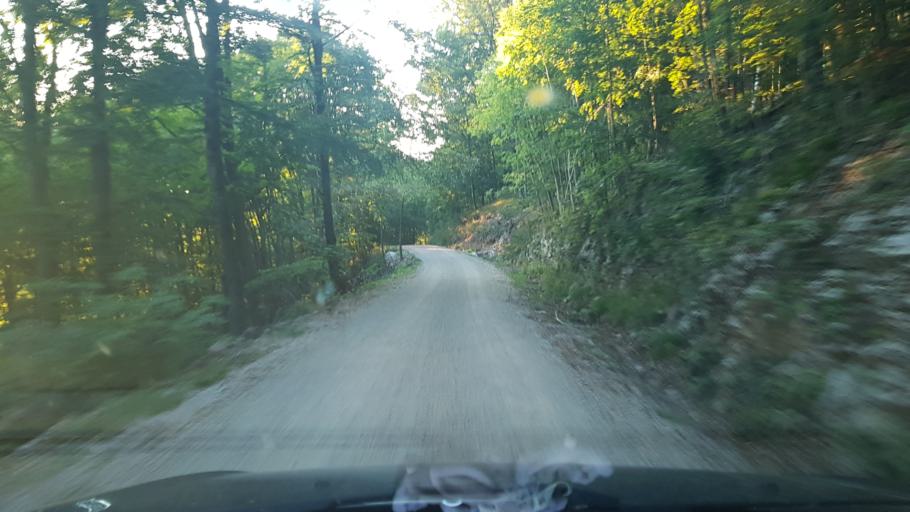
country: SI
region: Vipava
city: Vipava
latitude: 45.7812
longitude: 14.0416
